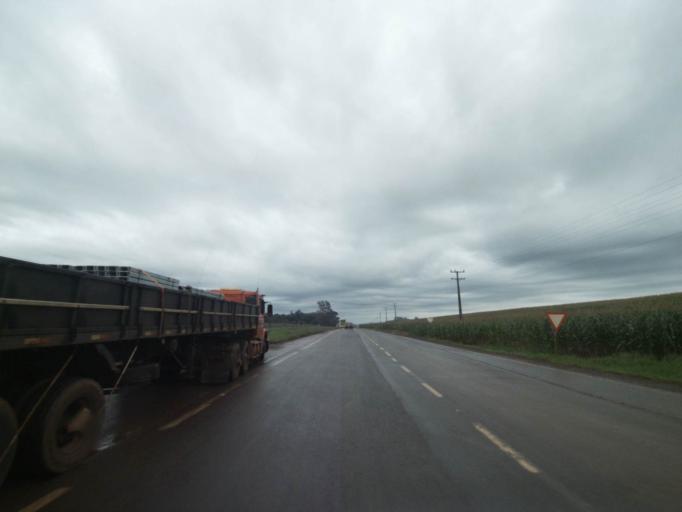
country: BR
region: Parana
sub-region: Toledo
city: Toledo
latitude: -24.6898
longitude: -53.7661
